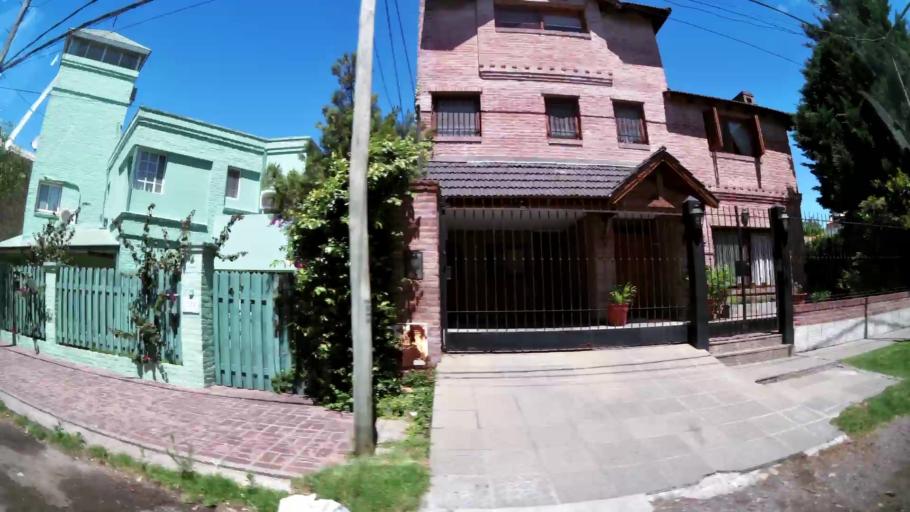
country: AR
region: Buenos Aires
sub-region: Partido de San Isidro
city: San Isidro
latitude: -34.4600
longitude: -58.5074
